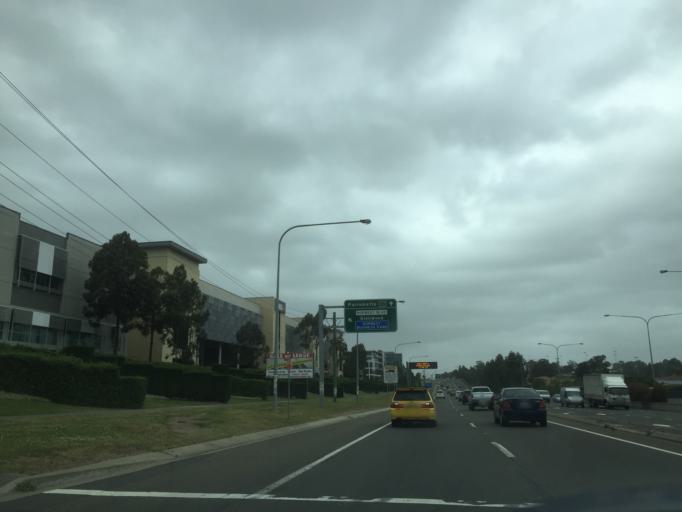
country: AU
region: New South Wales
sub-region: Blacktown
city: Stanhope Gardens
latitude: -33.7329
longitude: 150.9434
